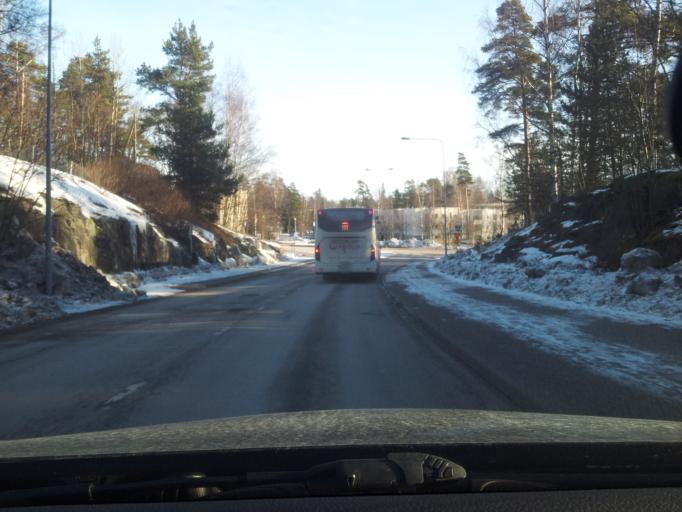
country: FI
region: Uusimaa
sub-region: Helsinki
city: Koukkuniemi
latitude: 60.1632
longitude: 24.7723
